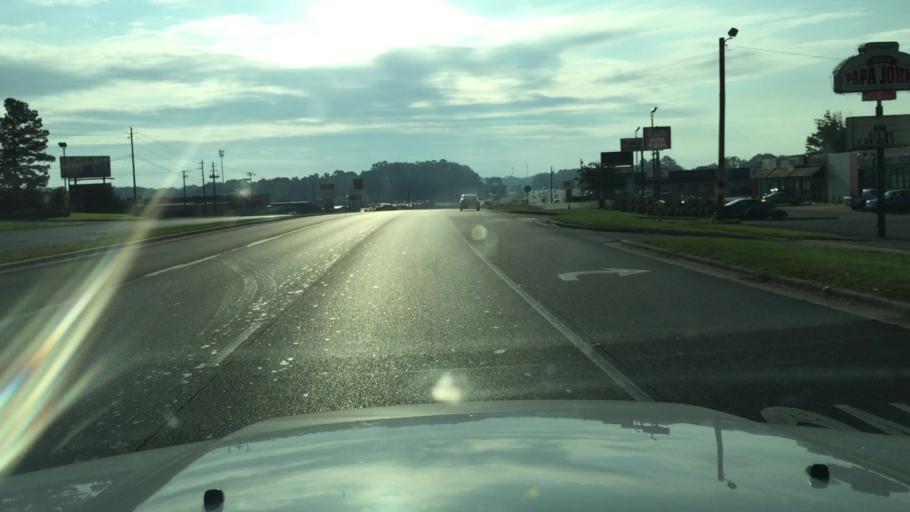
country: US
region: Alabama
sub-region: Tuscaloosa County
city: Northport
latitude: 33.2405
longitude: -87.5825
